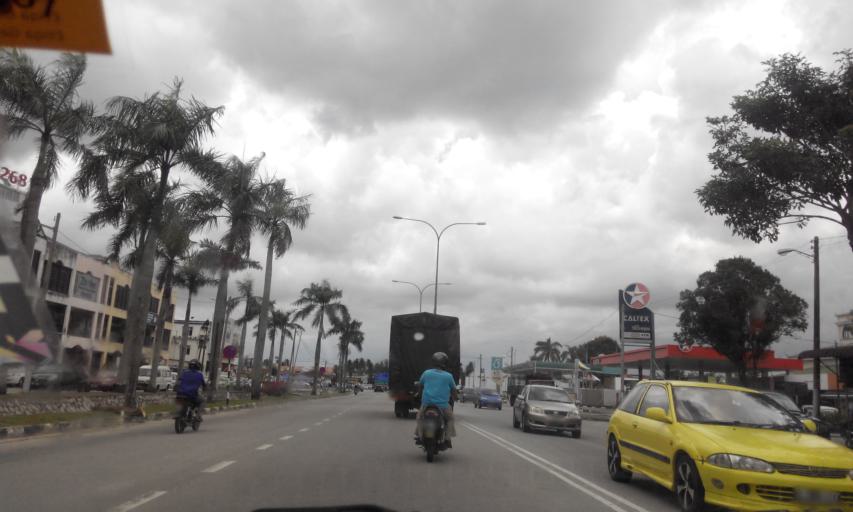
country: MY
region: Perak
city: Parit Buntar
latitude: 5.1149
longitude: 100.4856
